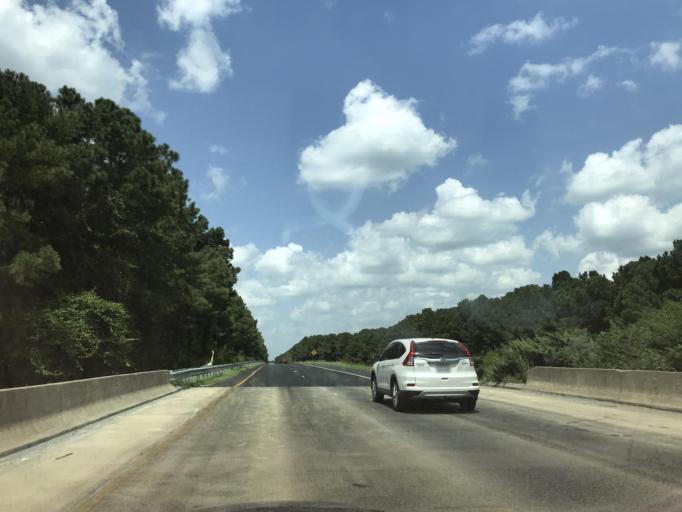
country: US
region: North Carolina
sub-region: Duplin County
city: Warsaw
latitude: 34.9933
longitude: -78.1326
